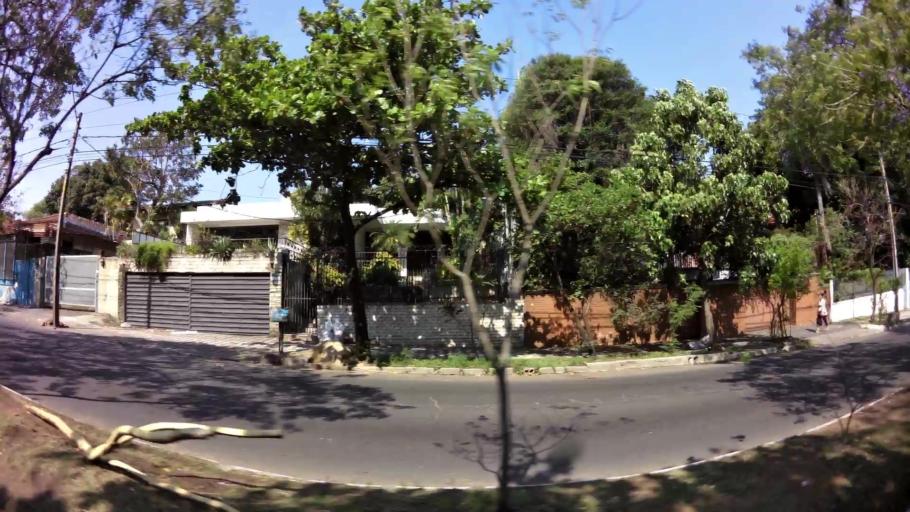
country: PY
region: Asuncion
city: Asuncion
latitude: -25.3049
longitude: -57.6320
